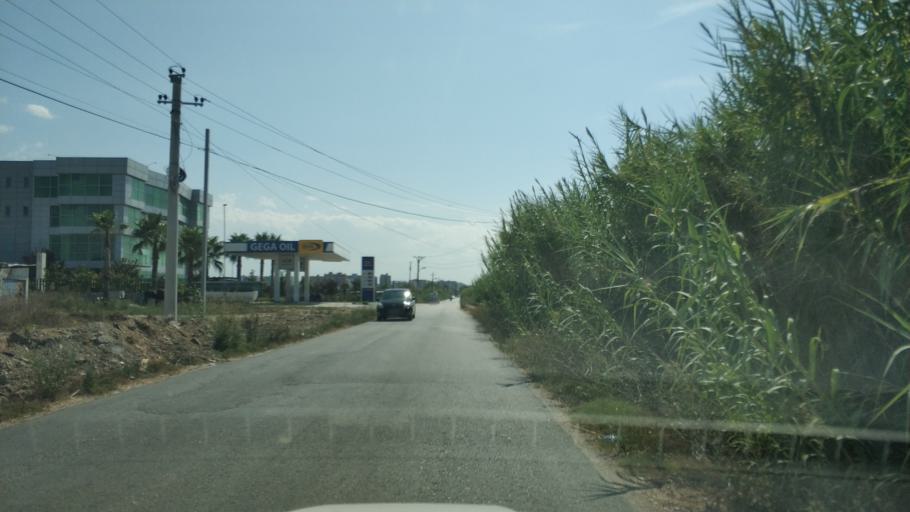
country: AL
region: Fier
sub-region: Rrethi i Fierit
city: Mbrostar-Ure
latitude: 40.7458
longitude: 19.5595
